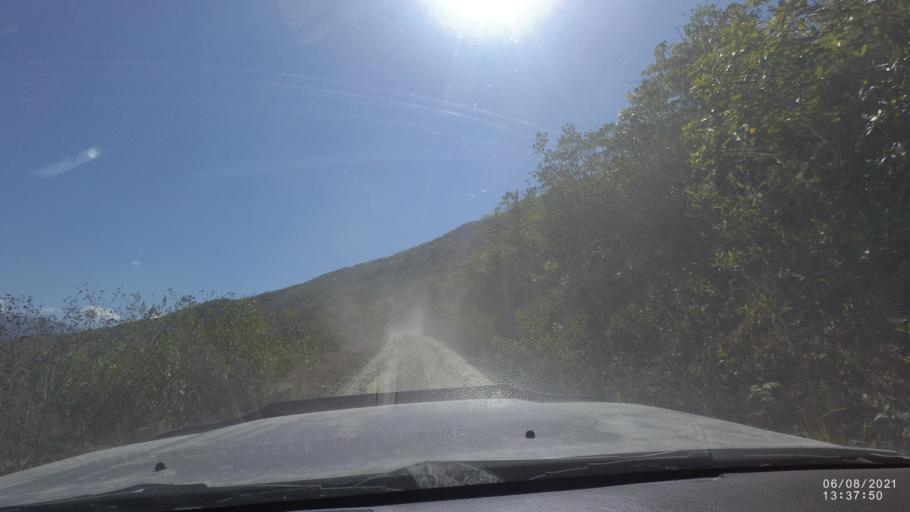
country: BO
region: La Paz
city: Quime
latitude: -16.6884
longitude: -66.7242
